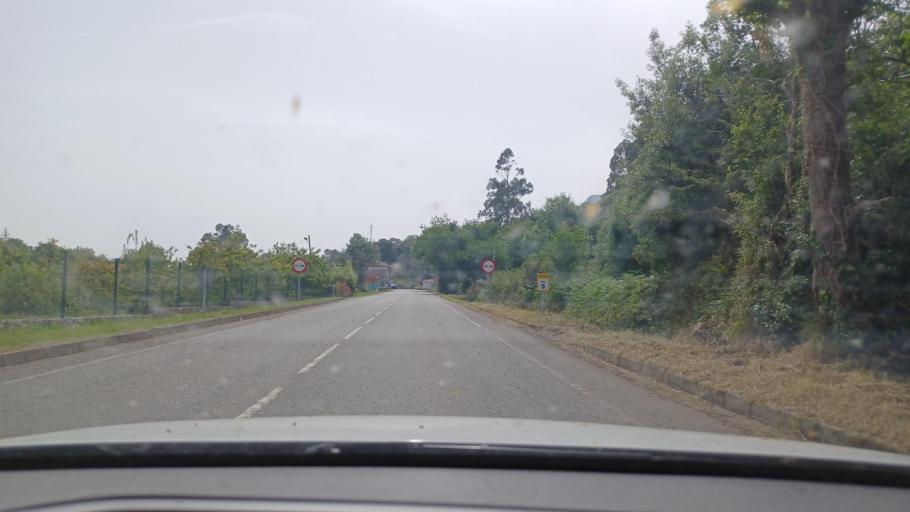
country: ES
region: Asturias
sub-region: Province of Asturias
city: Ribadesella
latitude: 43.4455
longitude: -5.0081
